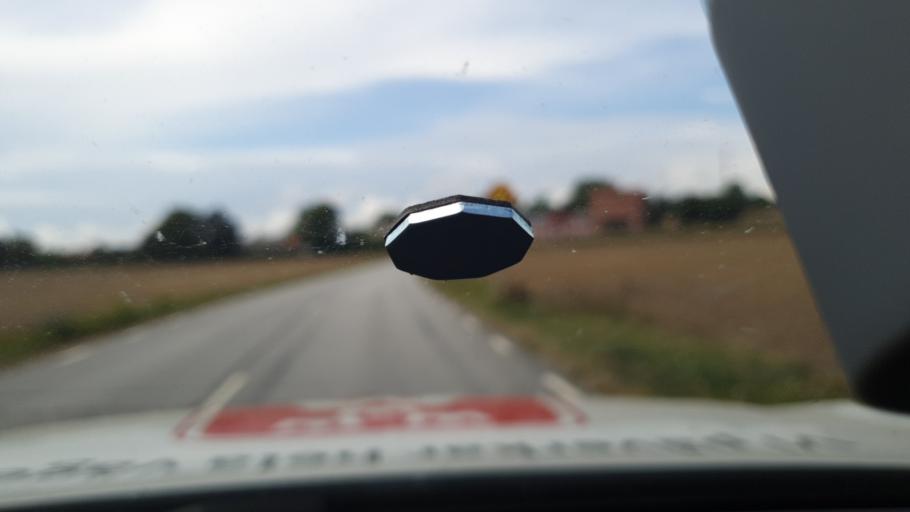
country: SE
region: Skane
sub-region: Simrishamns Kommun
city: Simrishamn
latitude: 55.4626
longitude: 14.1931
